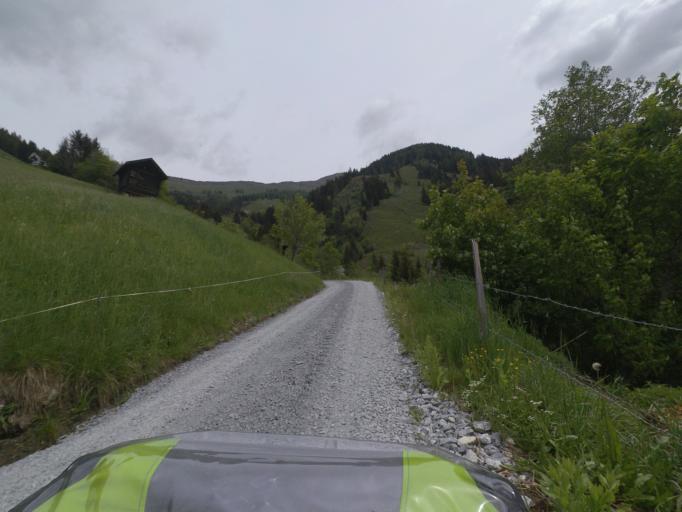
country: AT
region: Salzburg
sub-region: Politischer Bezirk Sankt Johann im Pongau
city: Dorfgastein
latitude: 47.2528
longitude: 13.1256
